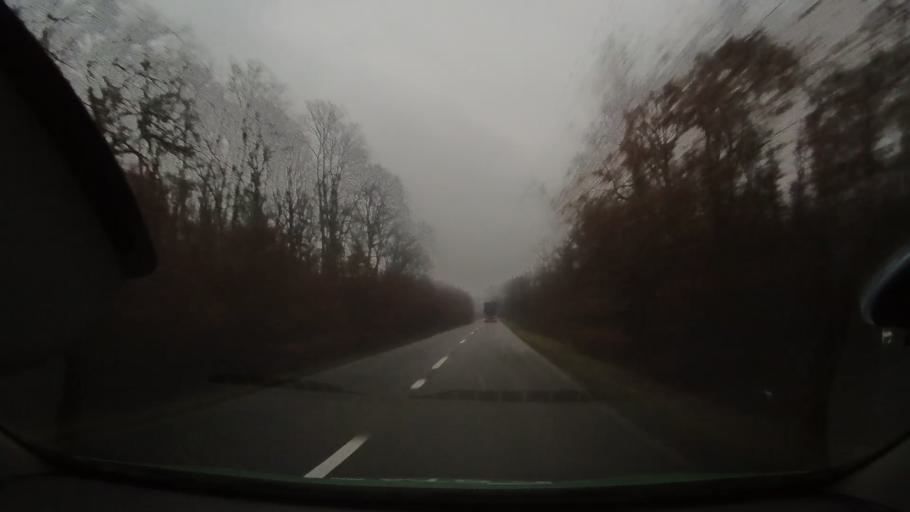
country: RO
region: Arad
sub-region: Comuna Beliu
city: Beliu
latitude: 46.5138
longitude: 21.9593
